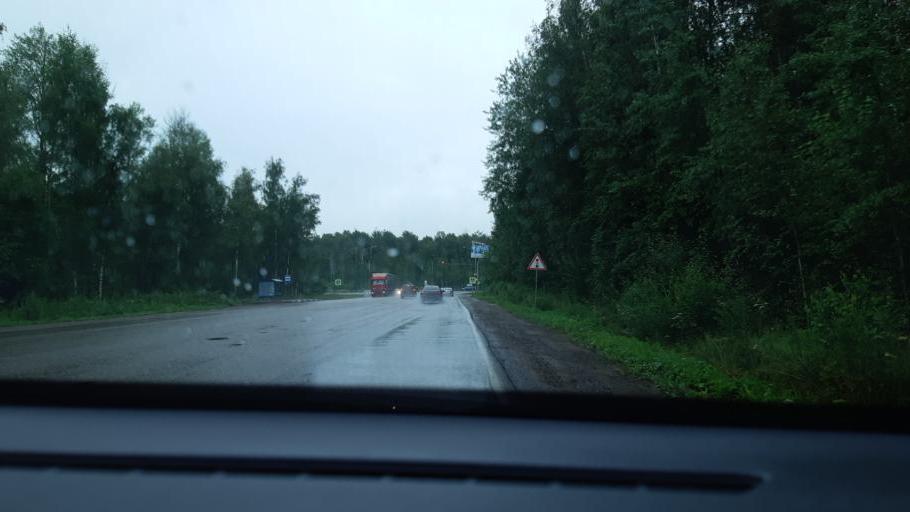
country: RU
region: Smolensk
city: Gagarin
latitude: 55.5014
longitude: 35.0363
